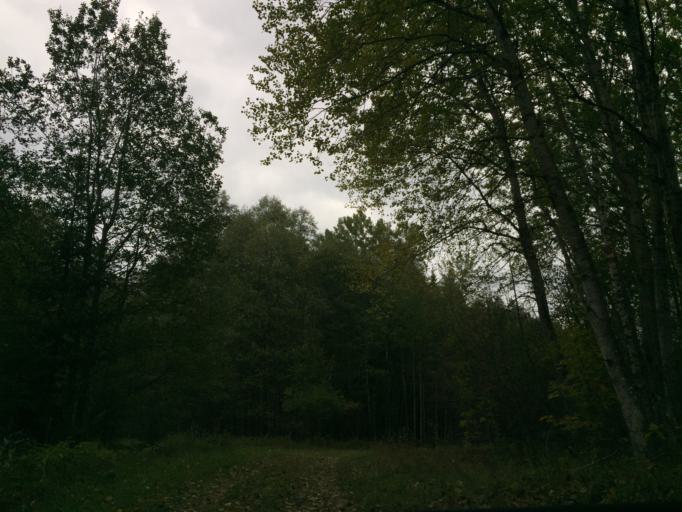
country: LV
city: Tireli
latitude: 56.8925
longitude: 23.5523
